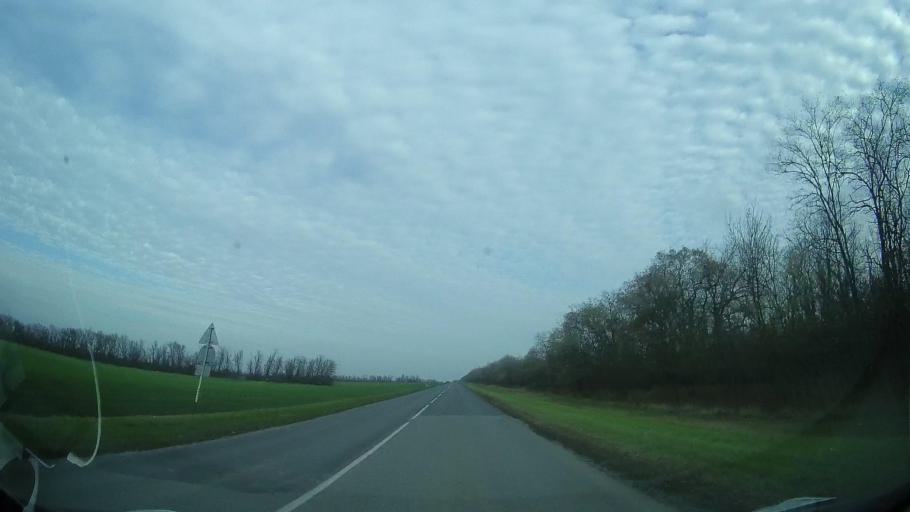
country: RU
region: Rostov
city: Zernograd
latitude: 46.9253
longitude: 40.3424
